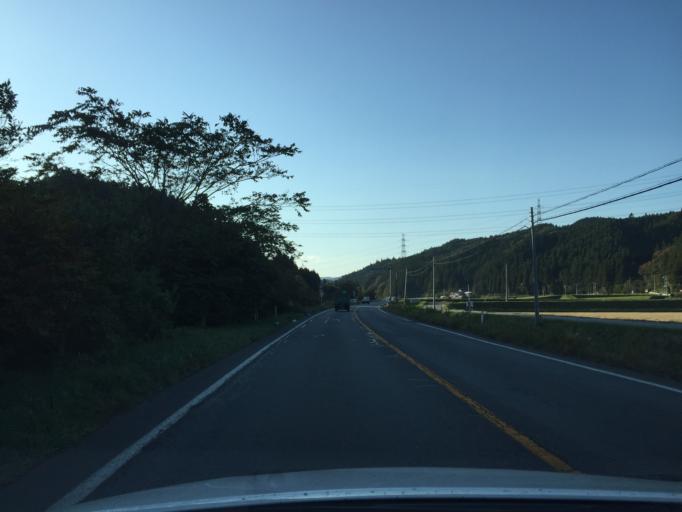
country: JP
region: Fukushima
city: Iwaki
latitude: 37.1323
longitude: 140.7144
